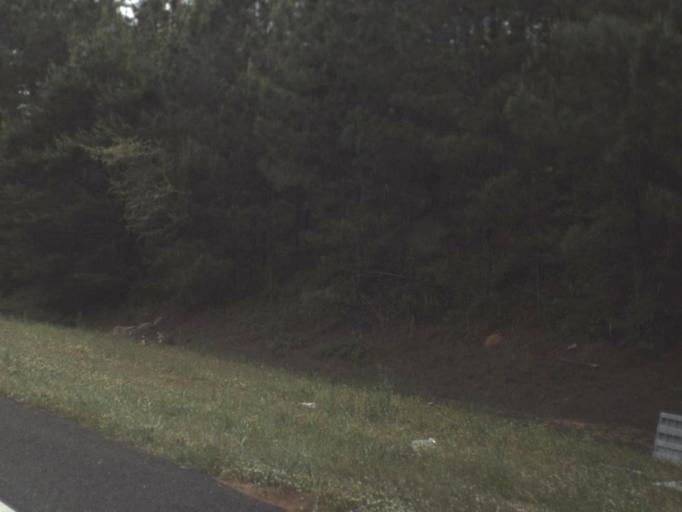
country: US
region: Florida
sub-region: Escambia County
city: Century
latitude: 30.9068
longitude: -87.3158
